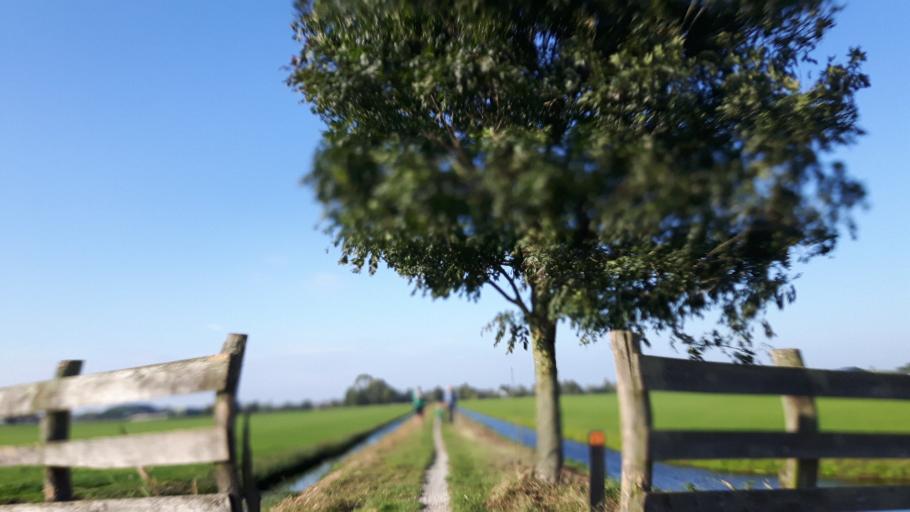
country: NL
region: Utrecht
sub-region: Gemeente Oudewater
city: Oudewater
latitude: 51.9810
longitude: 4.8875
